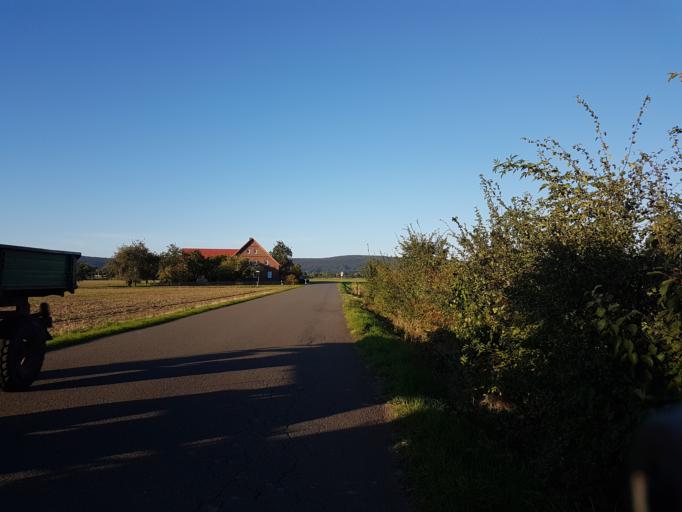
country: DE
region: North Rhine-Westphalia
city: Porta Westfalica
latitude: 52.1901
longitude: 8.9788
